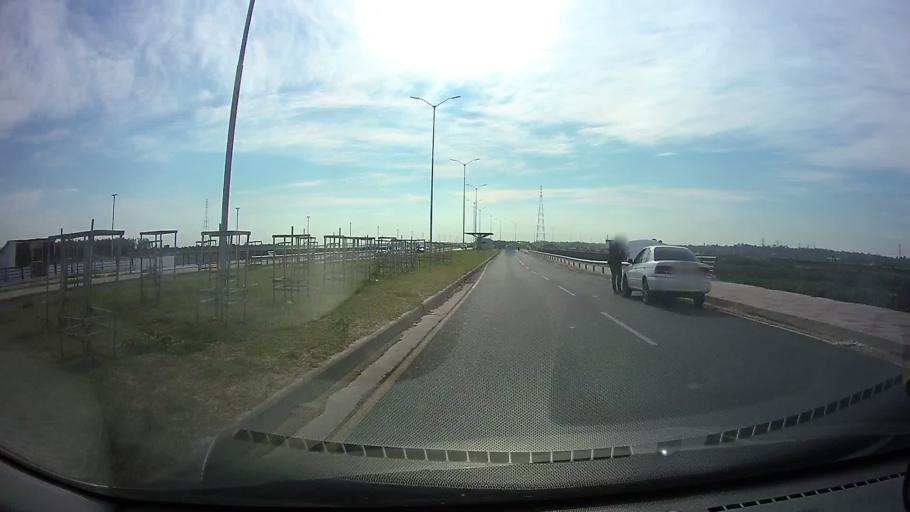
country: PY
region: Asuncion
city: Asuncion
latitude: -25.2485
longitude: -57.6006
